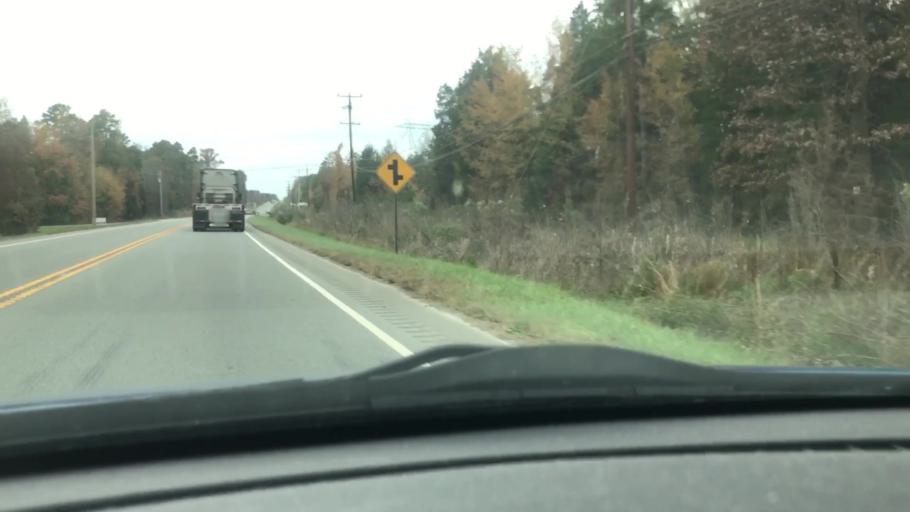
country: US
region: North Carolina
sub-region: Davidson County
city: Thomasville
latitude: 35.7786
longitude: -80.1194
